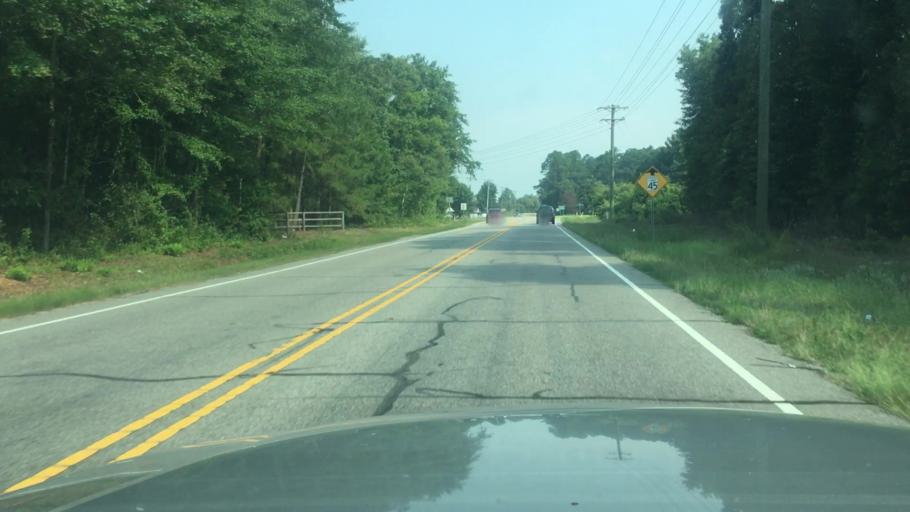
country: US
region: North Carolina
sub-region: Cumberland County
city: Hope Mills
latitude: 34.9138
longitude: -78.9069
